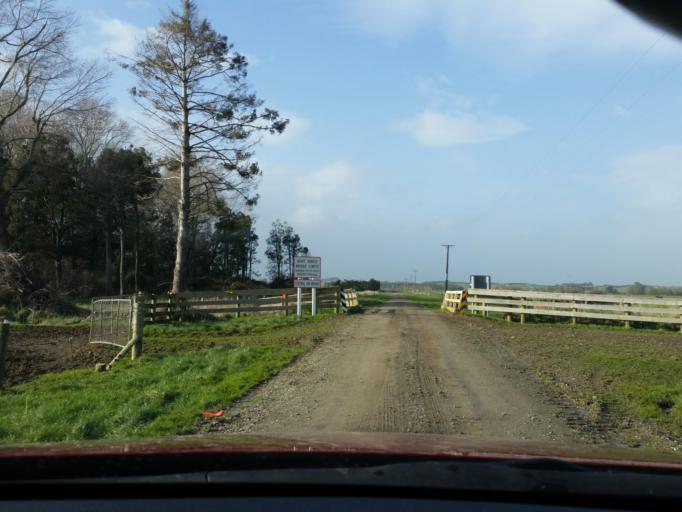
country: NZ
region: Southland
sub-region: Invercargill City
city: Invercargill
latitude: -46.2806
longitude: 168.4229
